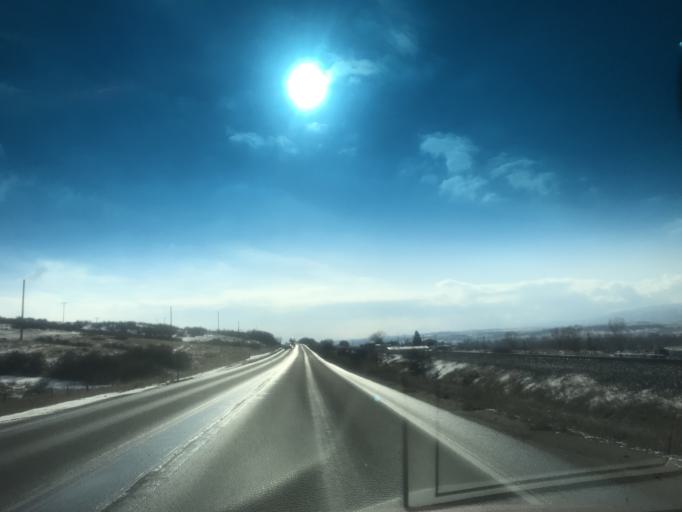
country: US
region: Colorado
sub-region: Douglas County
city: Highlands Ranch
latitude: 39.4682
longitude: -104.9879
